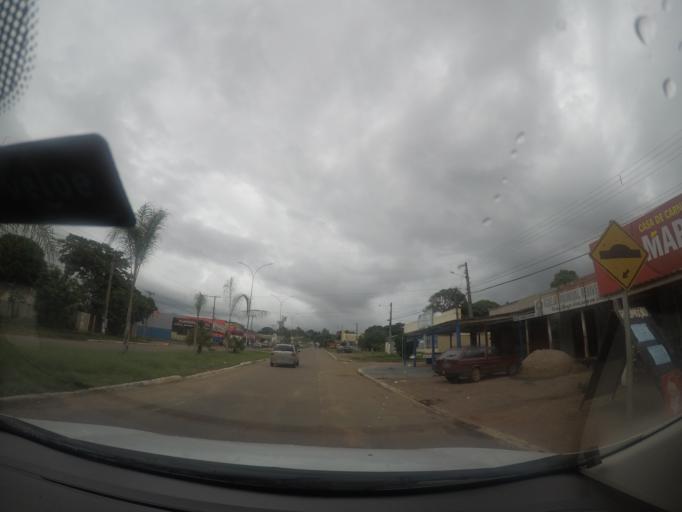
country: BR
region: Goias
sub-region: Trindade
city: Trindade
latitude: -16.6207
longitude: -49.3890
